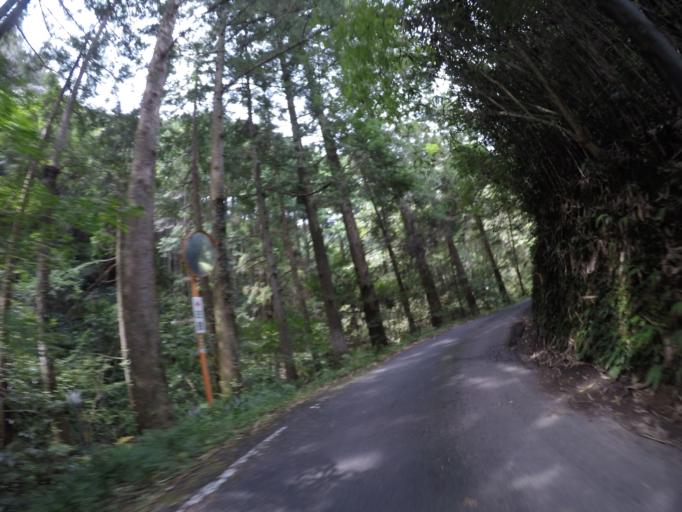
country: JP
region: Shizuoka
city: Shimada
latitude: 34.8774
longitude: 138.1747
